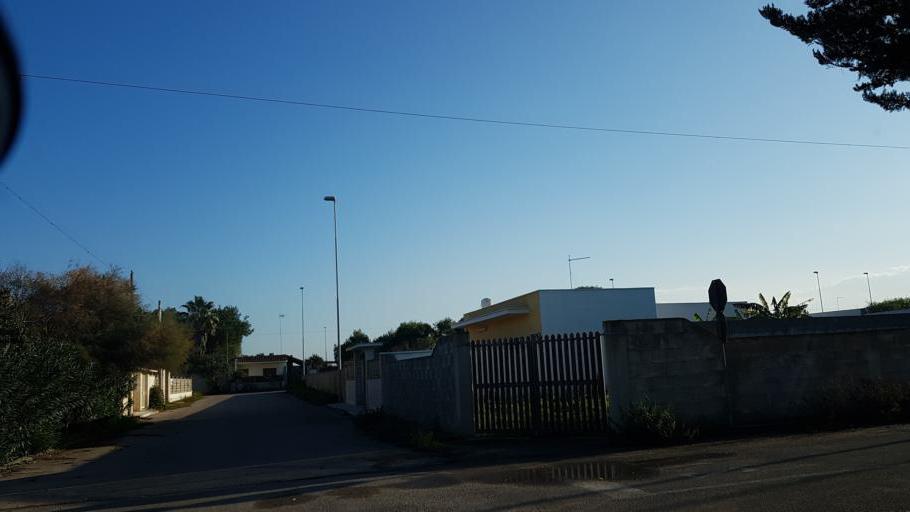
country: IT
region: Apulia
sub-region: Provincia di Brindisi
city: Torchiarolo
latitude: 40.5126
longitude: 18.0986
